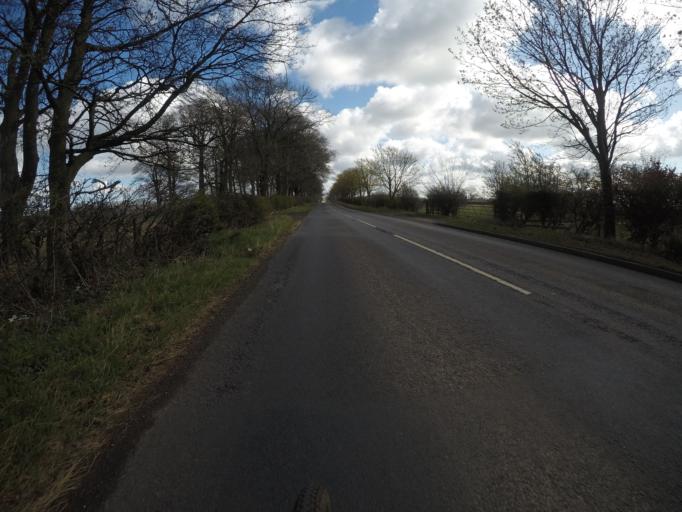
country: GB
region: Scotland
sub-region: North Ayrshire
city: Dreghorn
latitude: 55.5946
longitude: -4.6159
